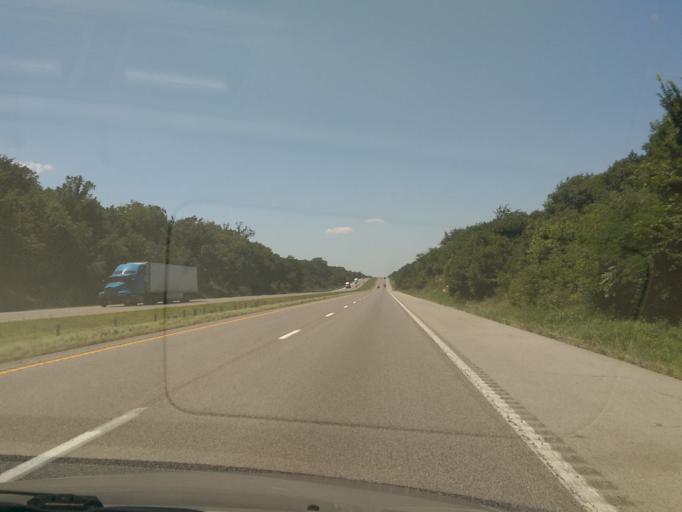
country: US
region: Missouri
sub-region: Saline County
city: Marshall
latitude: 38.9551
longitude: -93.1165
